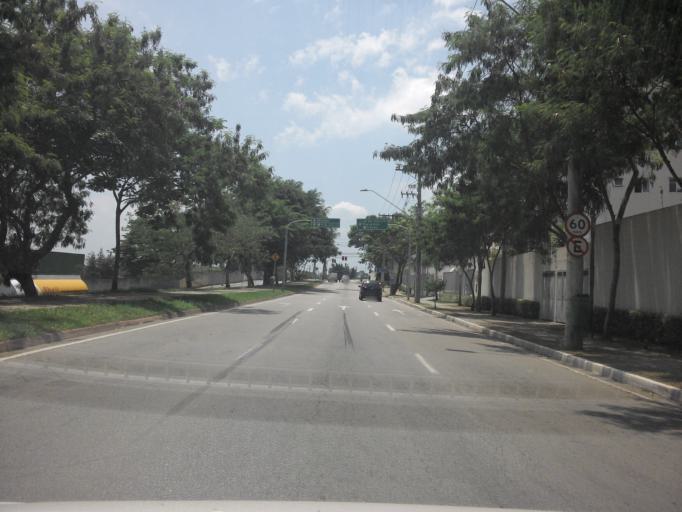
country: BR
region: Sao Paulo
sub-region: Sao Jose Dos Campos
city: Sao Jose dos Campos
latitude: -23.1653
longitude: -45.8069
